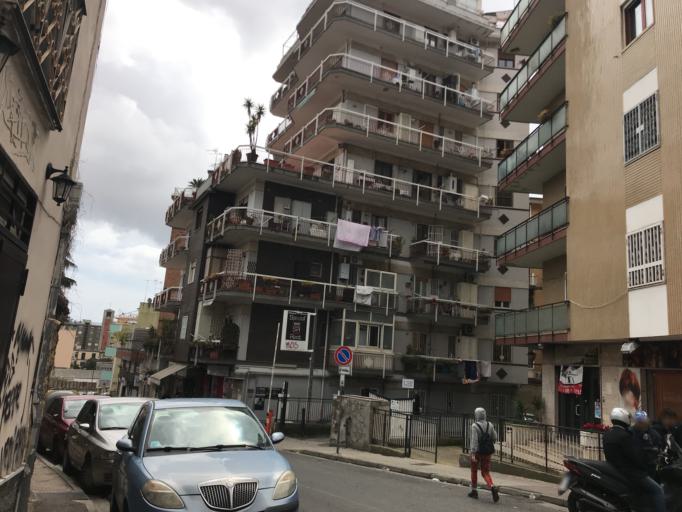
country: IT
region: Campania
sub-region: Provincia di Napoli
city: Napoli
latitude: 40.8552
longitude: 14.2233
